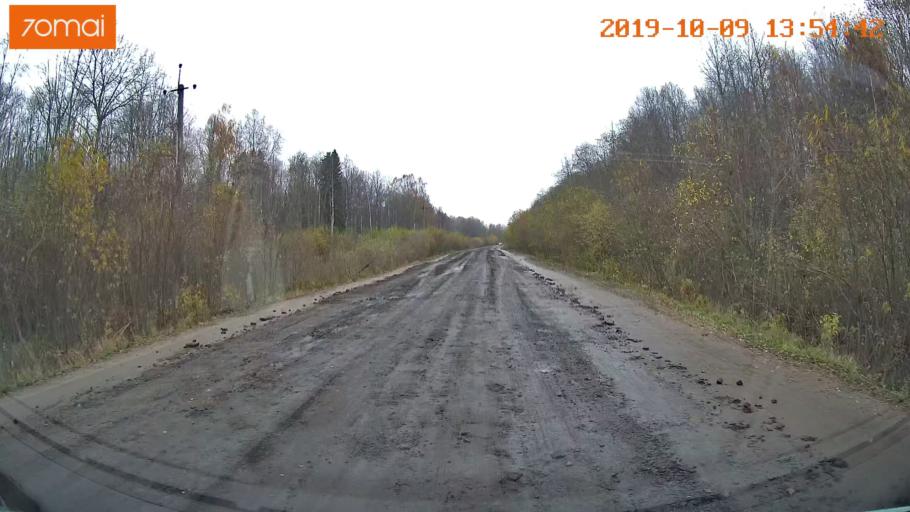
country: RU
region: Kostroma
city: Buy
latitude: 58.4217
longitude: 41.2686
